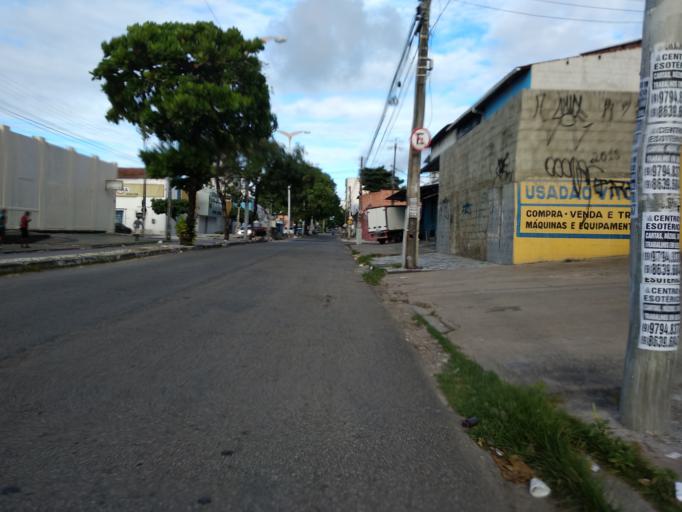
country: BR
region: Ceara
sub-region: Fortaleza
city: Fortaleza
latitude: -3.7294
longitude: -38.5378
